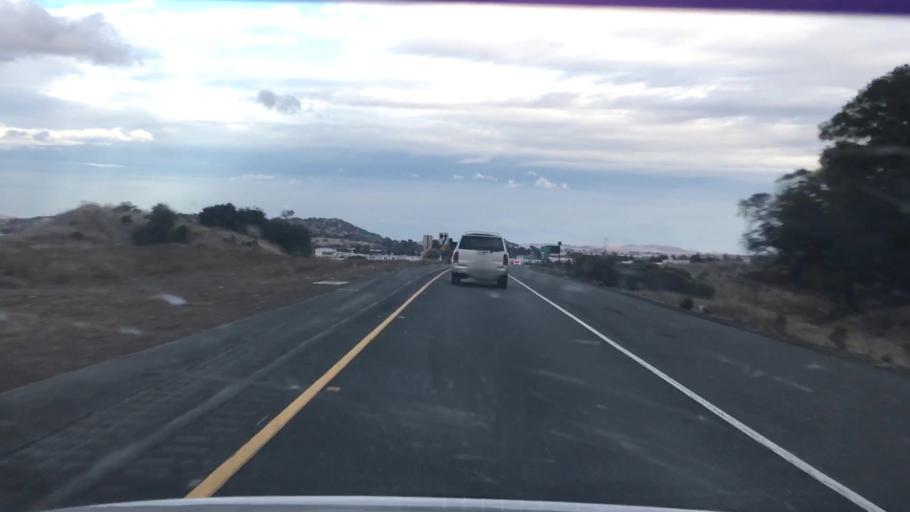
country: US
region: California
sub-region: Solano County
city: Green Valley
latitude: 38.2082
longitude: -122.1528
